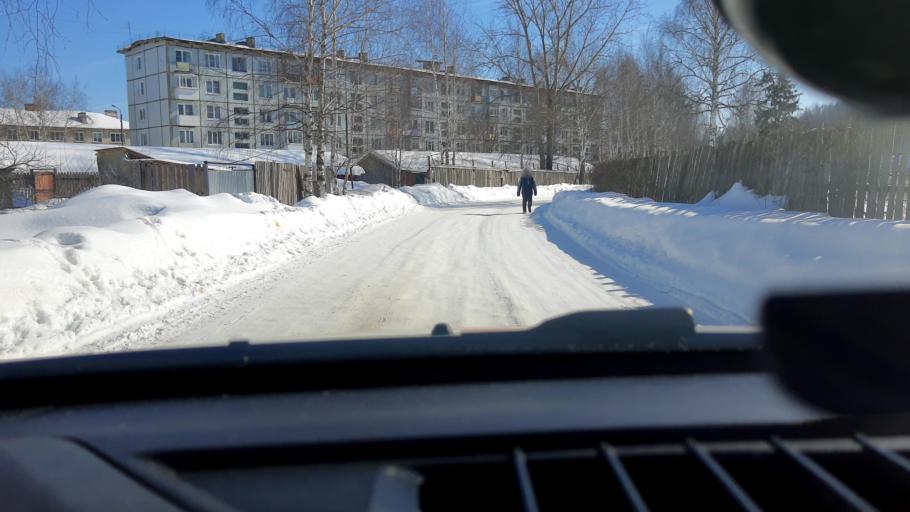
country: RU
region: Nizjnij Novgorod
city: Yuganets
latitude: 56.2471
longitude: 43.2269
